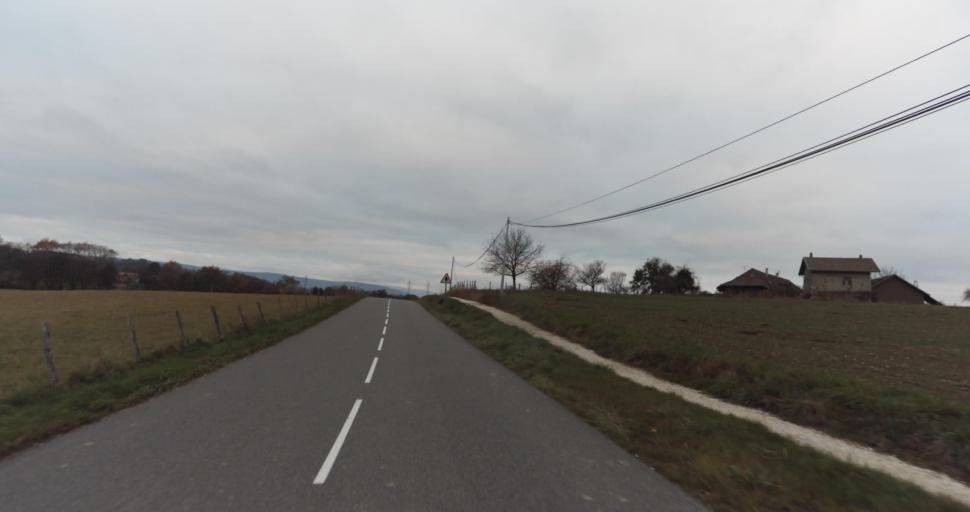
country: FR
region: Rhone-Alpes
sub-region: Departement de la Haute-Savoie
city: Chavanod
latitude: 45.8844
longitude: 6.0455
